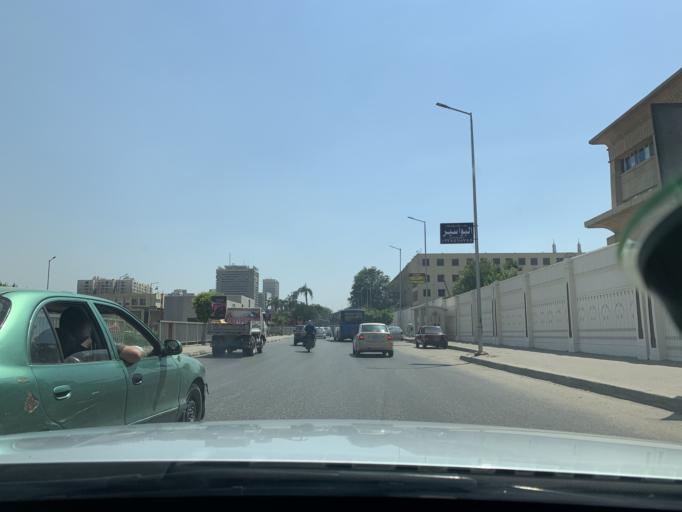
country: EG
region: Muhafazat al Qahirah
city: Cairo
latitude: 30.0777
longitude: 31.2890
